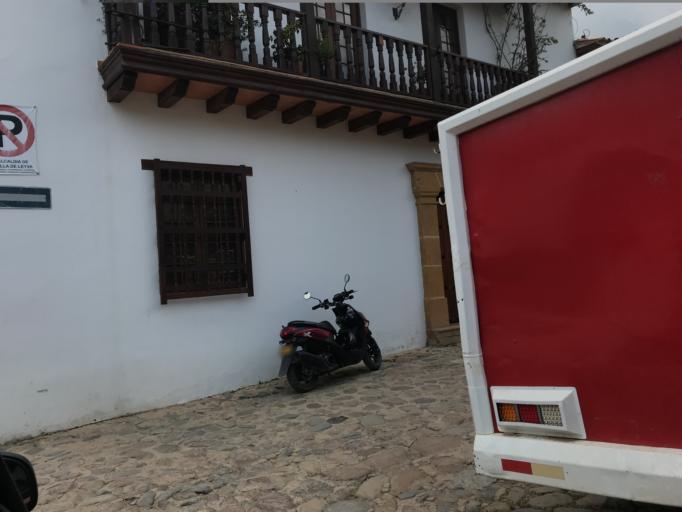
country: CO
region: Boyaca
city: Villa de Leiva
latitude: 5.6321
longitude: -73.5239
